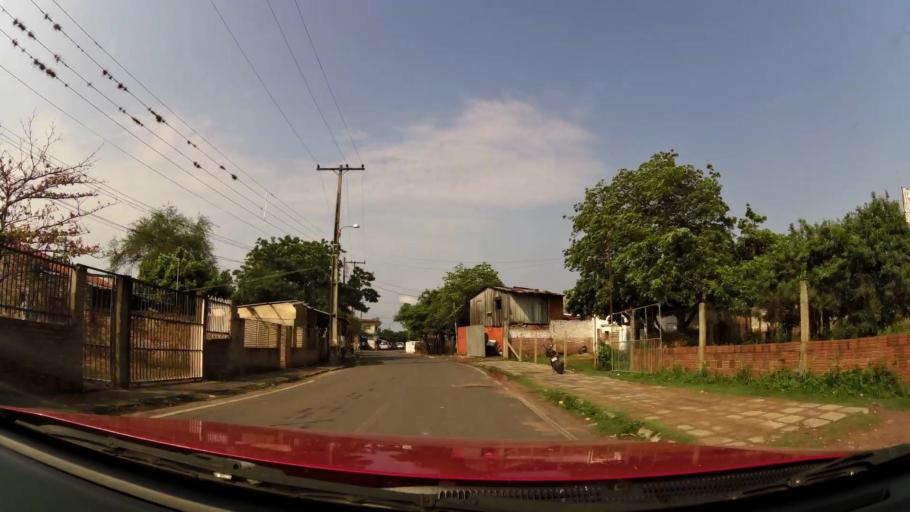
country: PY
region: Asuncion
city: Asuncion
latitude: -25.3135
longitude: -57.6681
